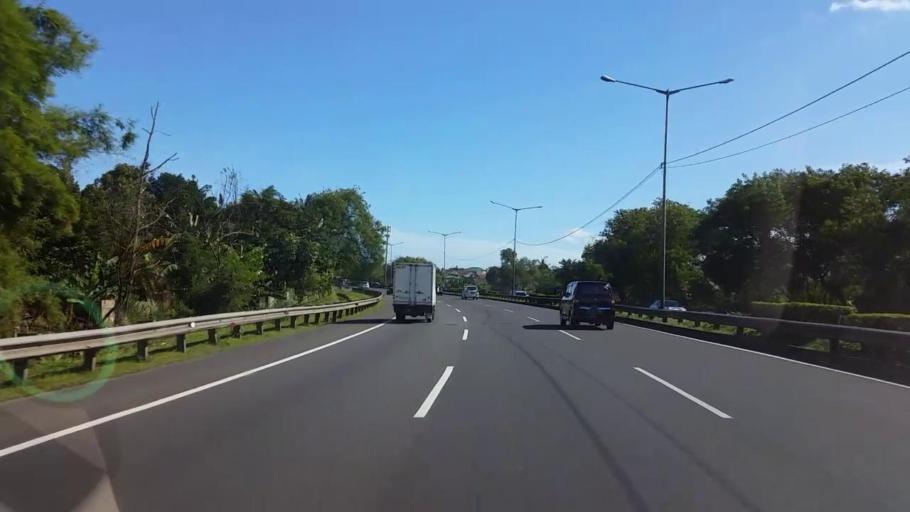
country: ID
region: Banten
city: South Tangerang
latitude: -6.2615
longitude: 106.7598
